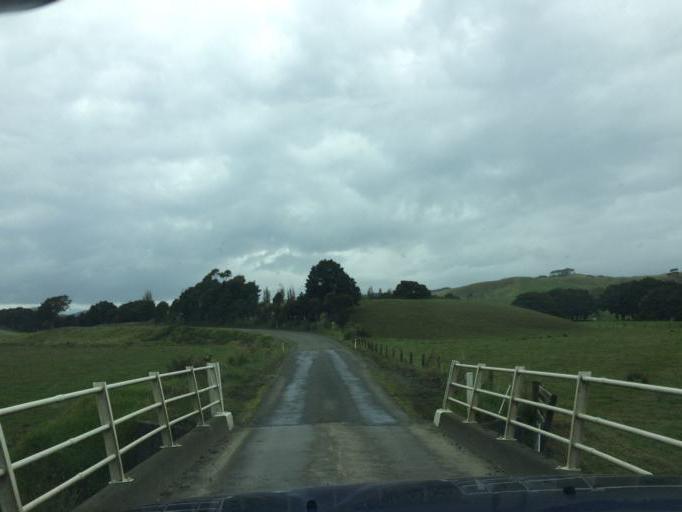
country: NZ
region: Northland
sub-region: Kaipara District
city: Dargaville
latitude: -35.8283
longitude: 173.8426
